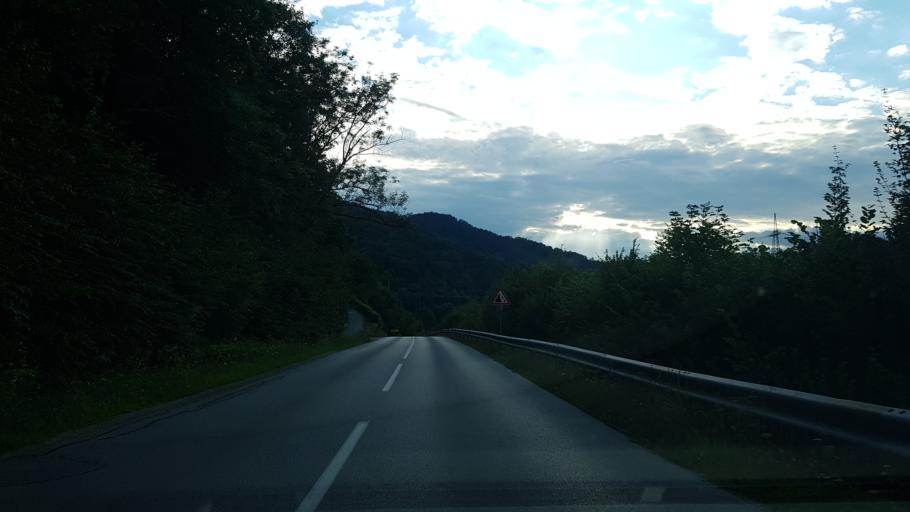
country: SI
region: Naklo
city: Naklo
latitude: 46.2494
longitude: 14.3305
